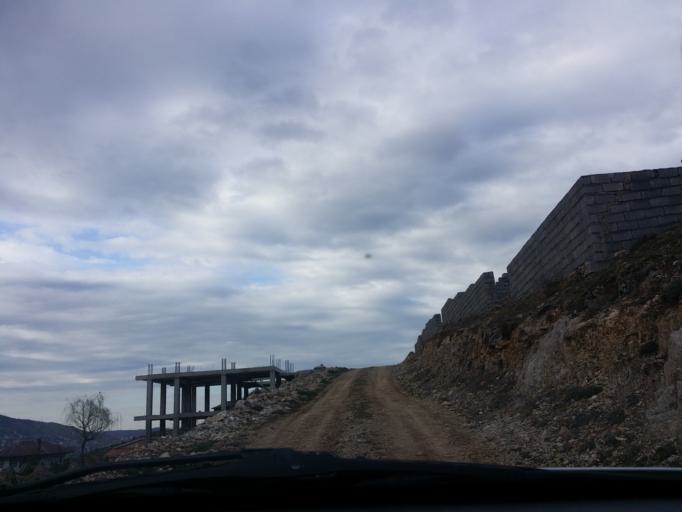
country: IR
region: Mazandaran
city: `Abbasabad
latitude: 36.4986
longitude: 51.1794
